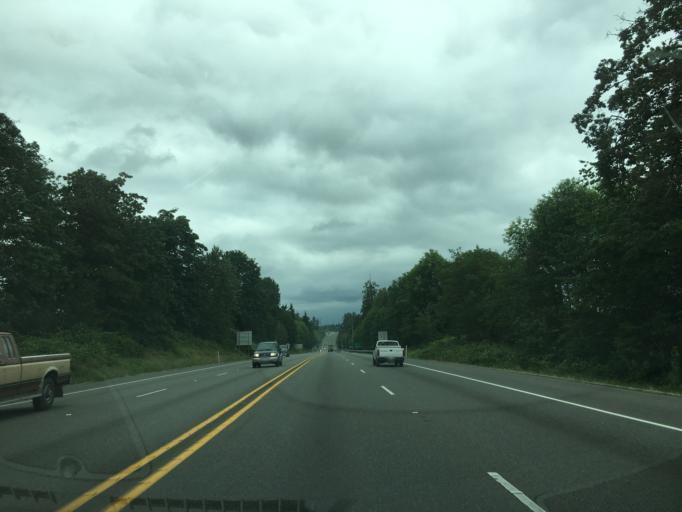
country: US
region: Washington
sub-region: Snohomish County
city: West Lake Stevens
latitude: 48.0076
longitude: -122.1071
